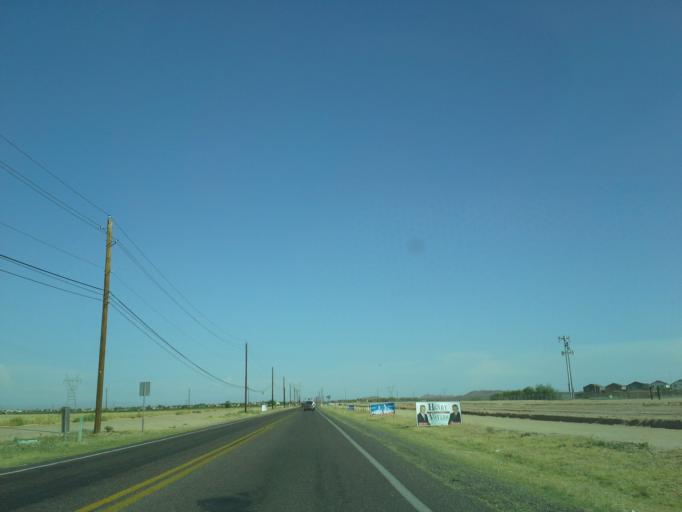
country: US
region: Arizona
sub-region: Pinal County
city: San Tan Valley
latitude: 33.1511
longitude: -111.5542
